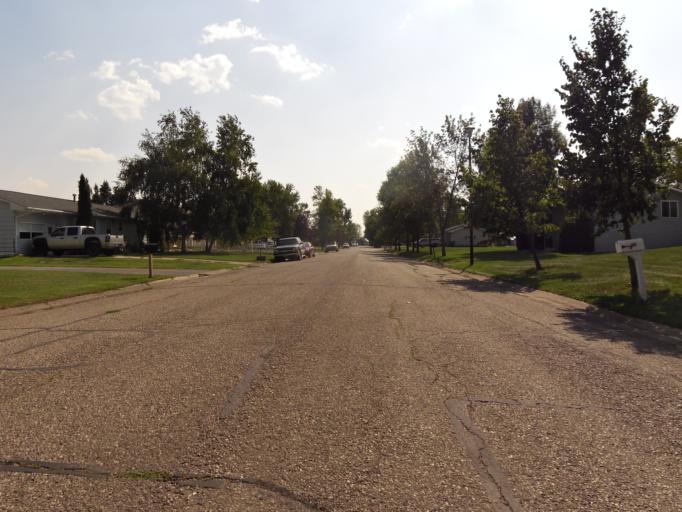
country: US
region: North Dakota
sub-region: Walsh County
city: Grafton
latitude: 48.4176
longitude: -97.3981
